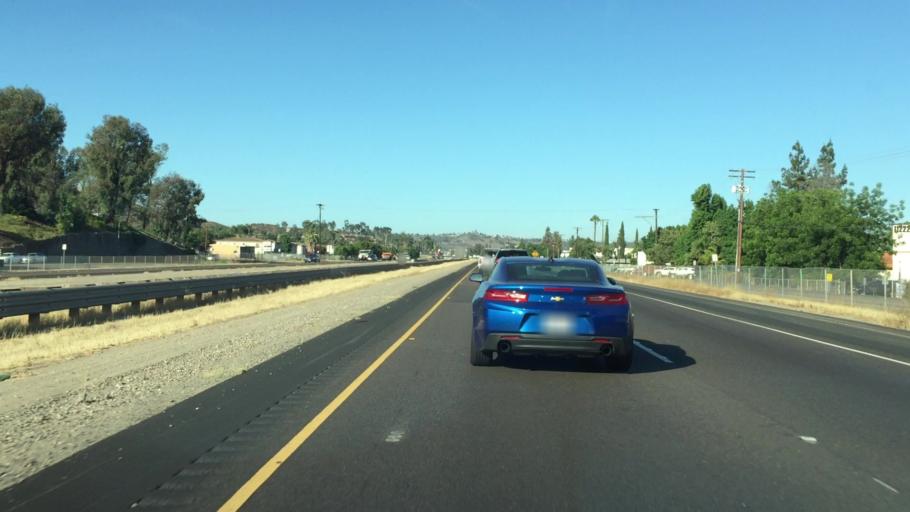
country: US
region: California
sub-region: San Diego County
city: Santee
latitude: 32.8486
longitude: -116.9545
